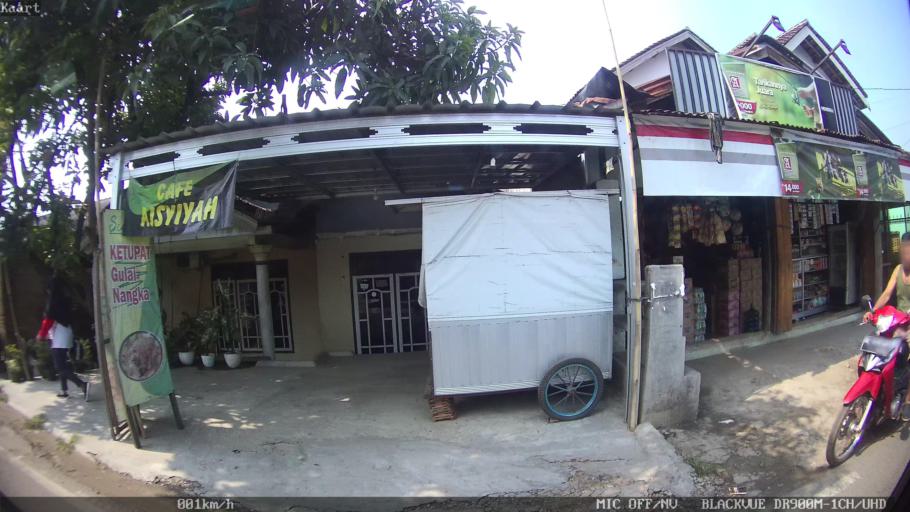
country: ID
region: Lampung
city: Gedongtataan
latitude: -5.3799
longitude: 105.0958
